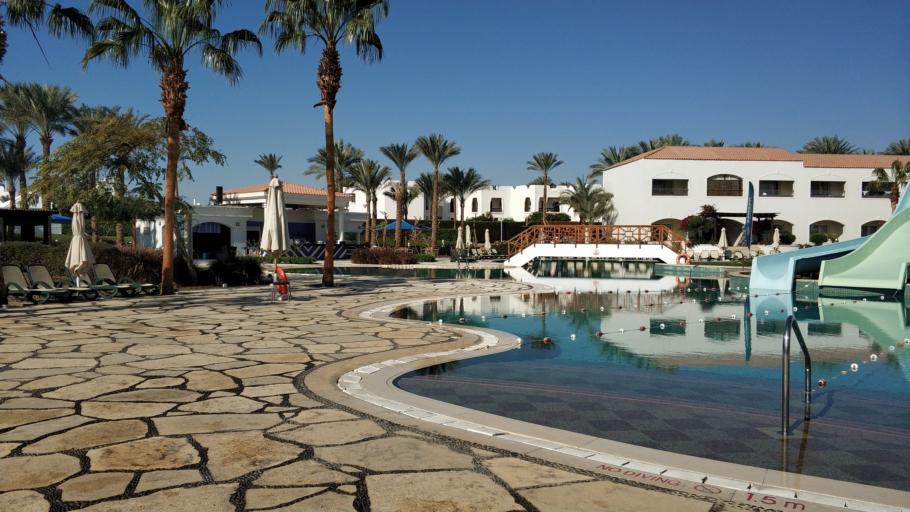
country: EG
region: South Sinai
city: Sharm el-Sheikh
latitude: 27.9198
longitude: 34.3611
